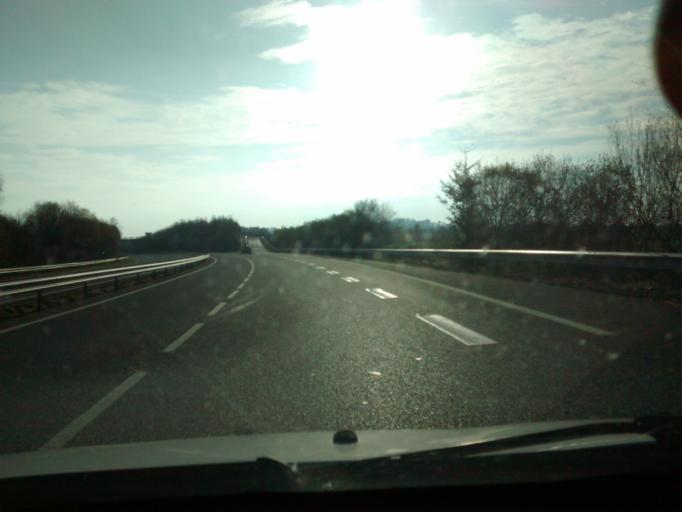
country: FR
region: Brittany
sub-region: Departement d'Ille-et-Vilaine
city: Chasne-sur-Illet
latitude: 48.2808
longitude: -1.5999
